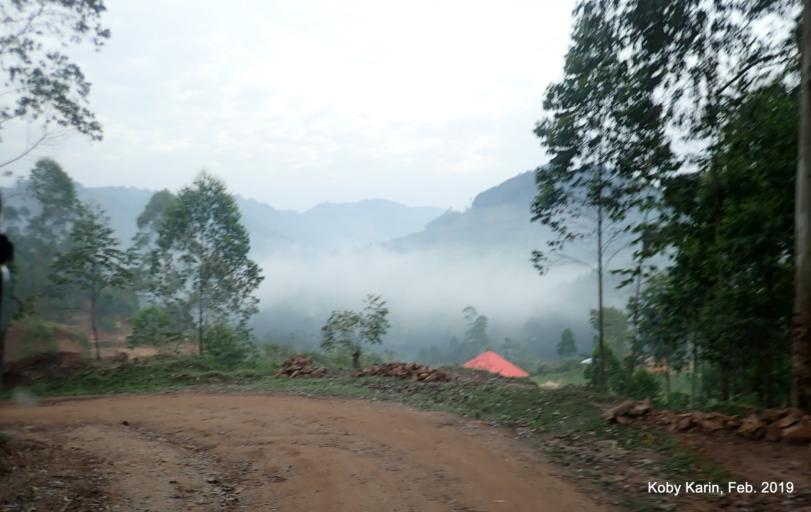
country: UG
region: Western Region
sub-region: Kisoro District
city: Kisoro
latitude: -1.1300
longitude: 29.7169
